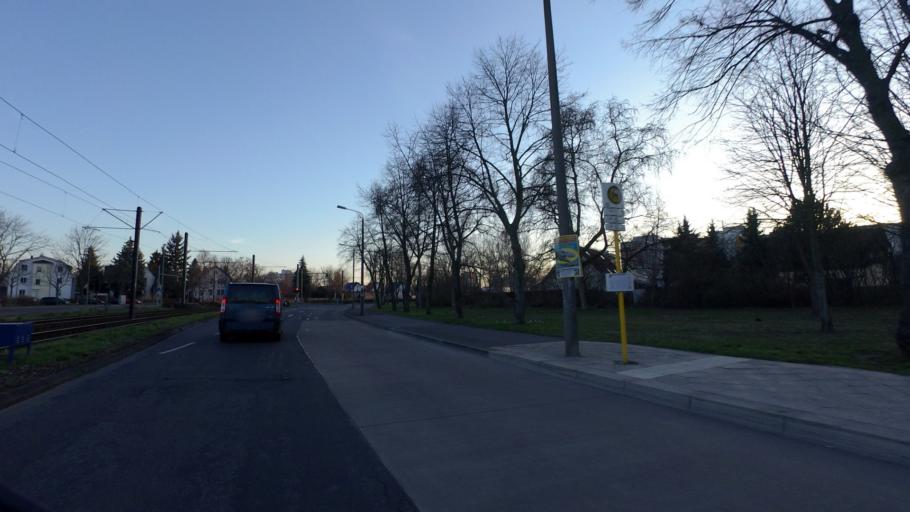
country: DE
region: Berlin
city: Marzahn
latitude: 52.5351
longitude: 13.5578
